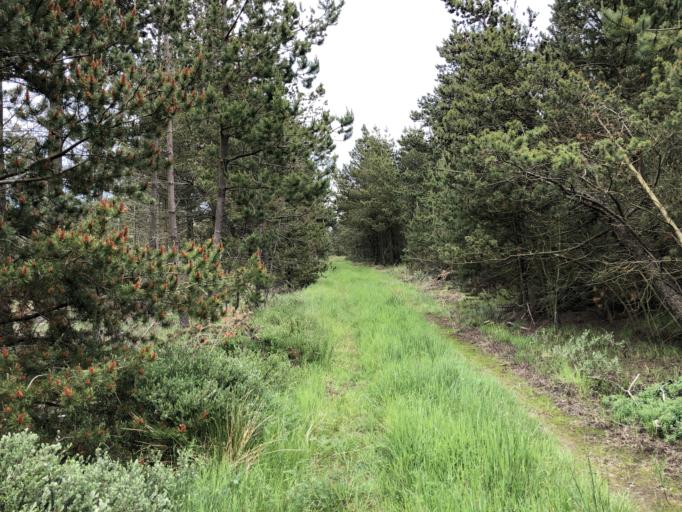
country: DK
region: Central Jutland
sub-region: Holstebro Kommune
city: Ulfborg
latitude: 56.2769
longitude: 8.3596
